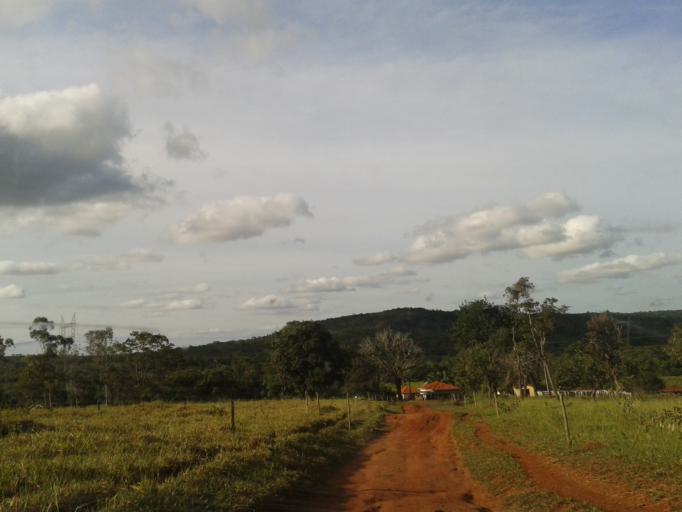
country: BR
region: Minas Gerais
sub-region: Campina Verde
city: Campina Verde
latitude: -19.4216
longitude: -49.7390
